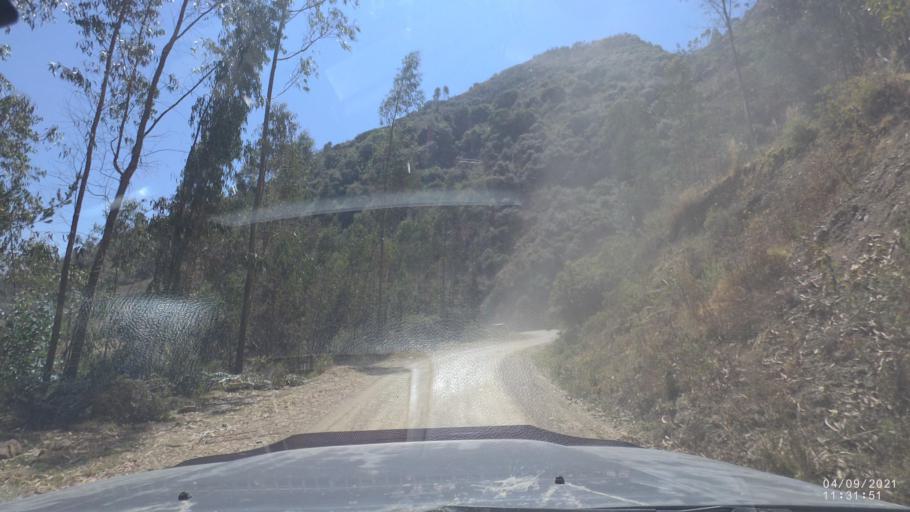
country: BO
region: Cochabamba
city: Colchani
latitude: -17.2312
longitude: -66.5207
